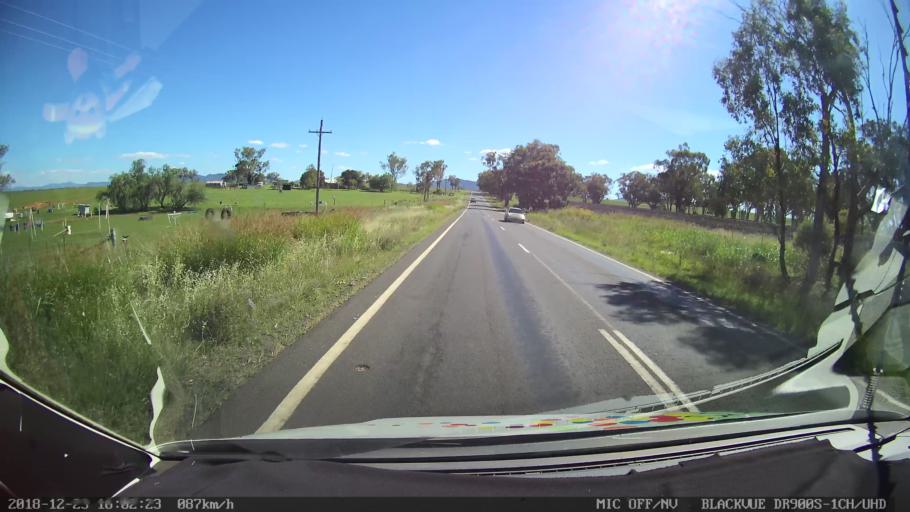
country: AU
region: New South Wales
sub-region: Tamworth Municipality
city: Phillip
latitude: -31.2316
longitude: 150.8095
